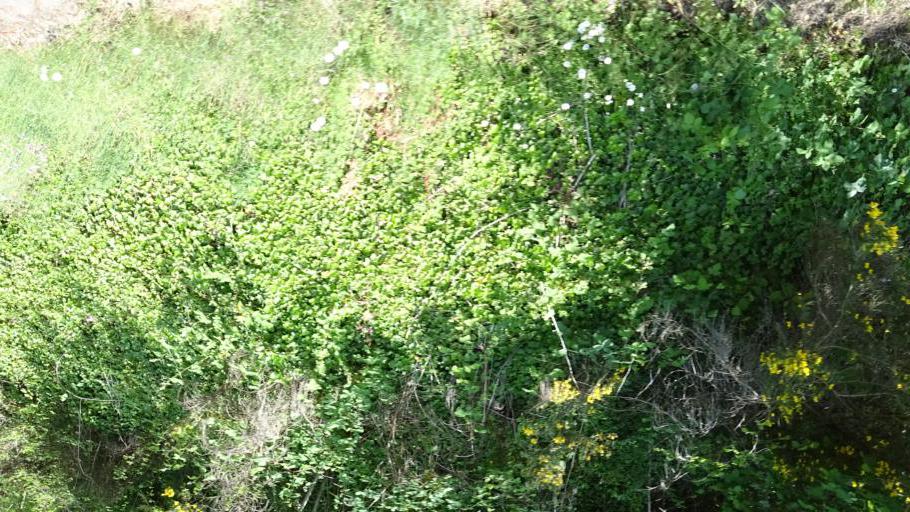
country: US
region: Oregon
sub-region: Multnomah County
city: Portland
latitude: 45.4918
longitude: -122.7024
